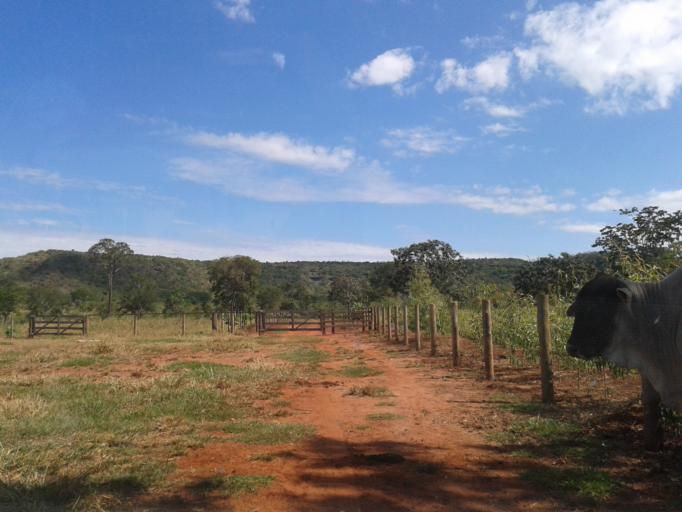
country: BR
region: Minas Gerais
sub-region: Campina Verde
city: Campina Verde
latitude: -19.4038
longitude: -49.7477
